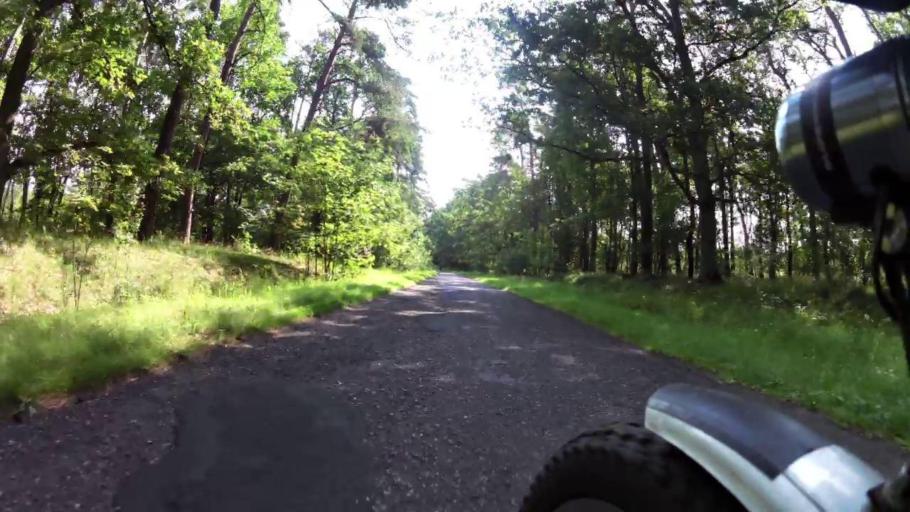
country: DE
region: Brandenburg
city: Zechin
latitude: 52.6756
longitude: 14.4978
